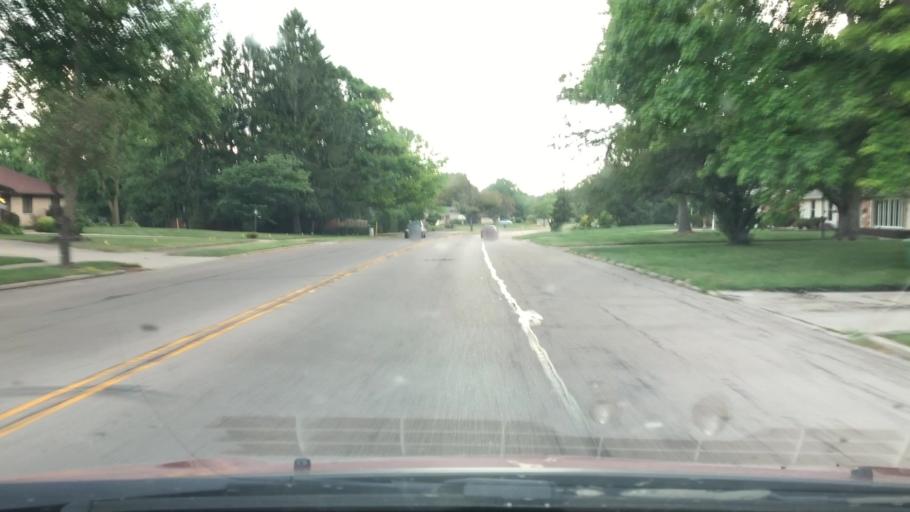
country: US
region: Ohio
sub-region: Greene County
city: Bellbrook
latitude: 39.6618
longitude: -84.1169
